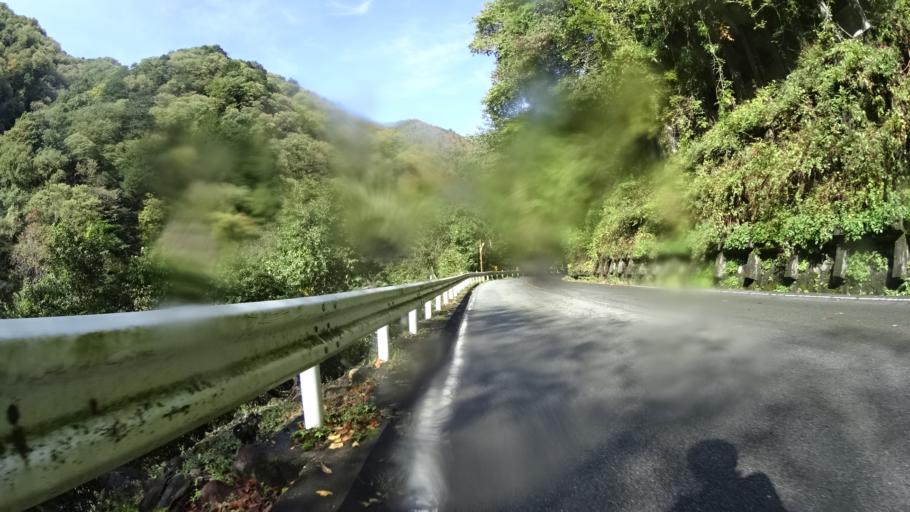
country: JP
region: Yamanashi
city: Enzan
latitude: 35.7951
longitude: 138.8666
